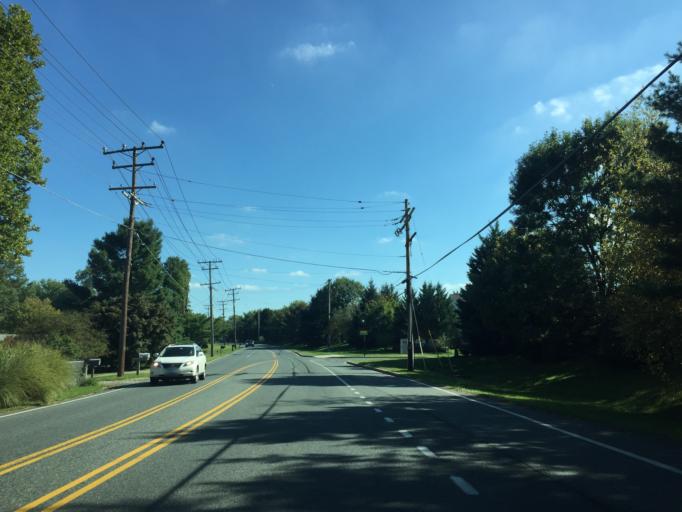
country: US
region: Maryland
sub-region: Harford County
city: Bel Air North
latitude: 39.5781
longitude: -76.3643
